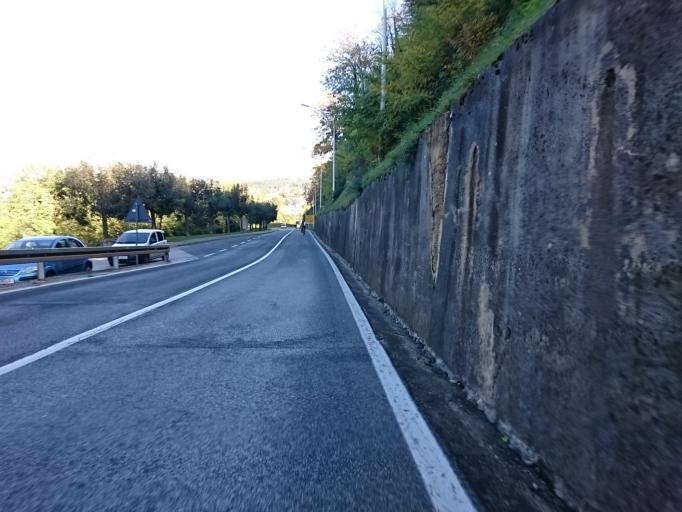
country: HR
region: Istarska
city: Buje
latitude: 45.4096
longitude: 13.6602
